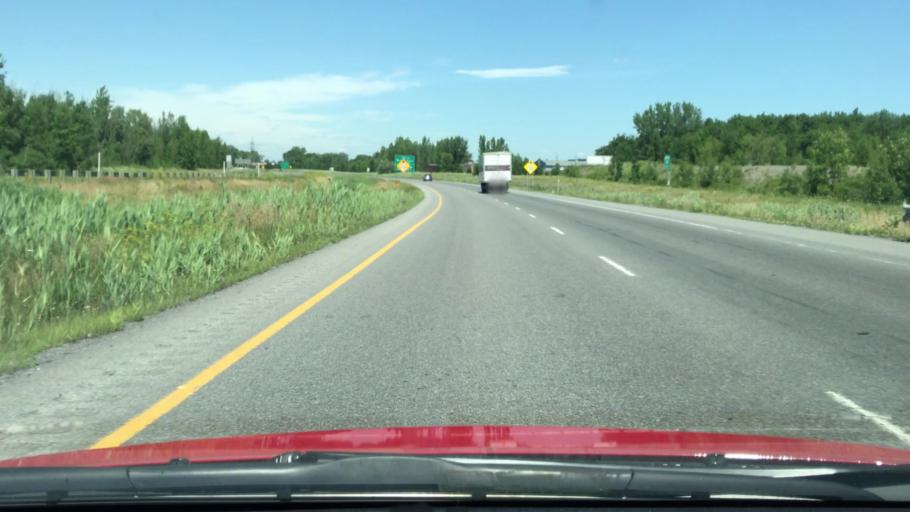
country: CA
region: Quebec
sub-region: Monteregie
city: Saint-Constant
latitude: 45.3886
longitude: -73.6052
